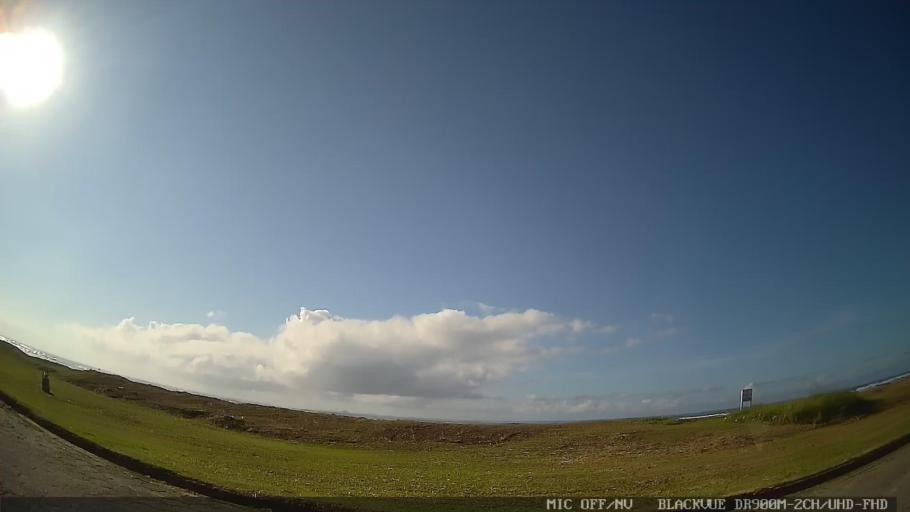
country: BR
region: Sao Paulo
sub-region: Peruibe
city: Peruibe
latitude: -24.2801
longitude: -46.9423
